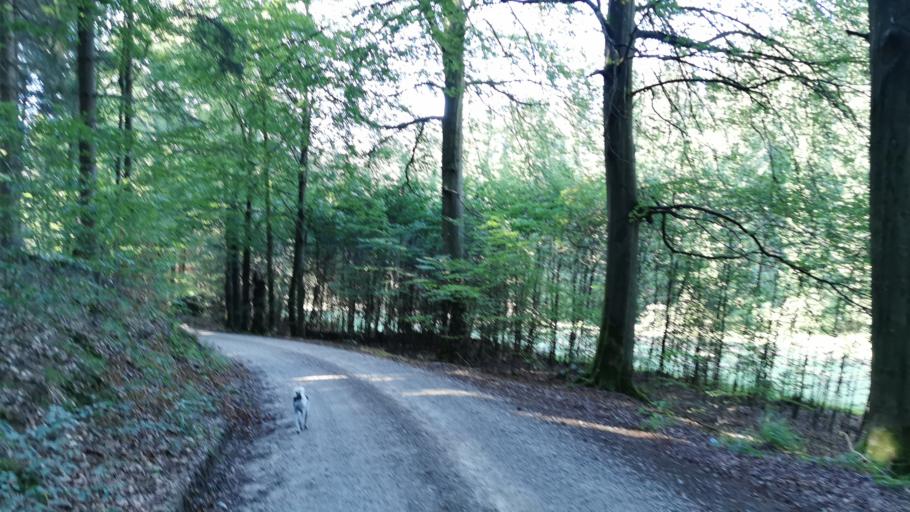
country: DE
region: Bavaria
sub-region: Upper Franconia
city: Nordhalben
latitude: 50.4121
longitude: 11.5385
